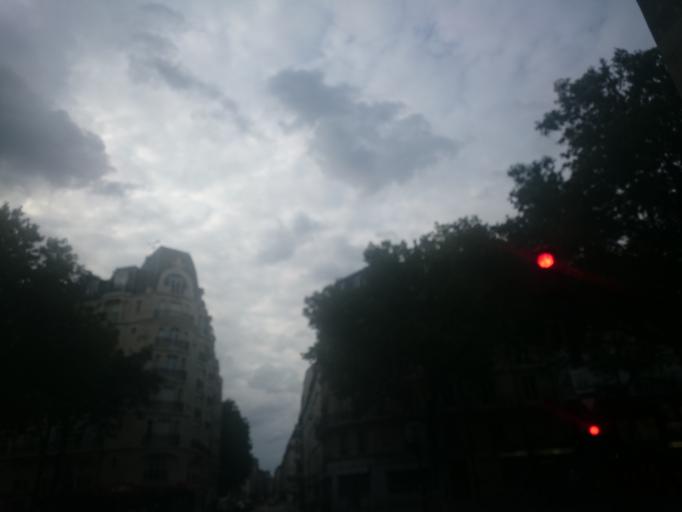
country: FR
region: Ile-de-France
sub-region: Departement du Val-de-Marne
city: Saint-Mande
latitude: 48.8478
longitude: 2.3930
